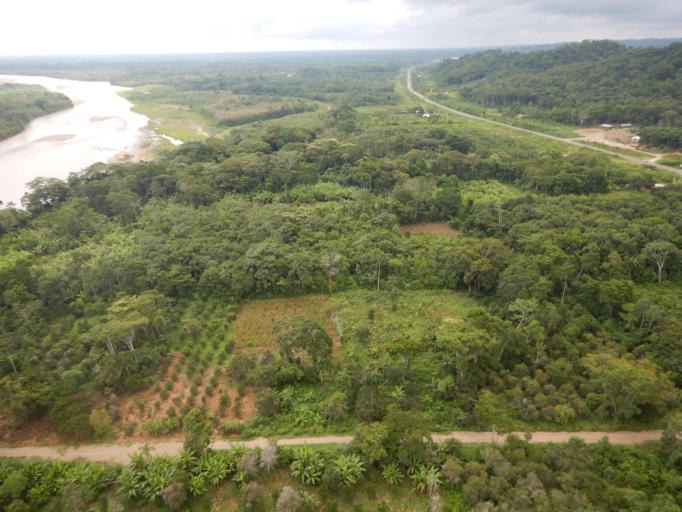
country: BO
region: Cochabamba
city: Chimore
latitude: -16.9908
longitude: -65.1127
